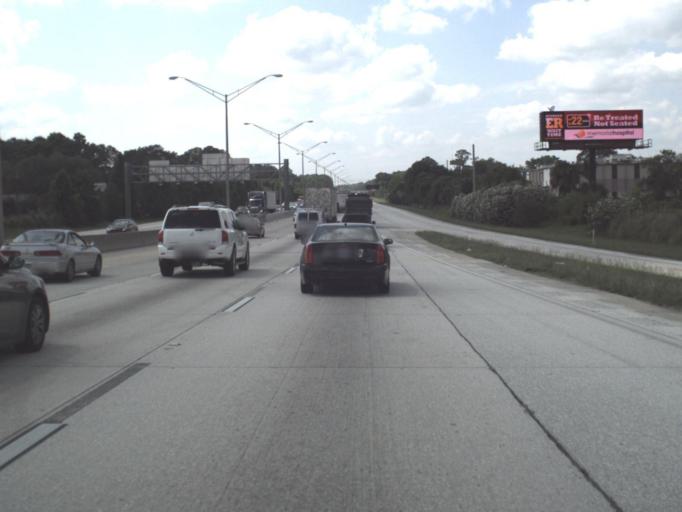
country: US
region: Florida
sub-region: Duval County
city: Jacksonville
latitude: 30.2708
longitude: -81.6130
